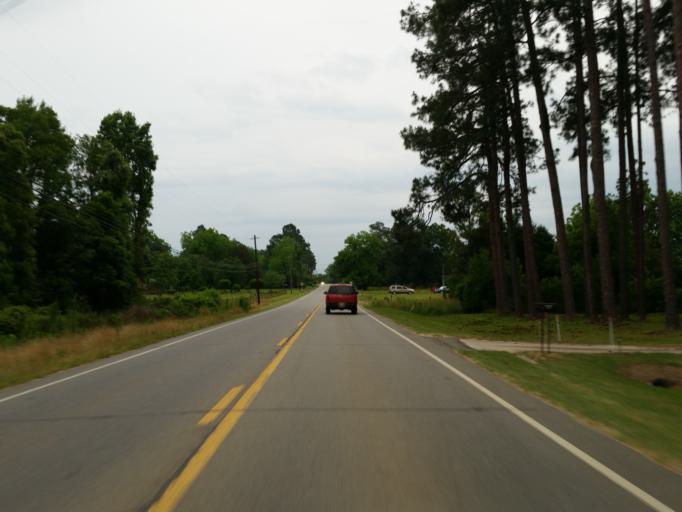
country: US
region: Georgia
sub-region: Dooly County
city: Vienna
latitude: 32.1085
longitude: -83.7983
